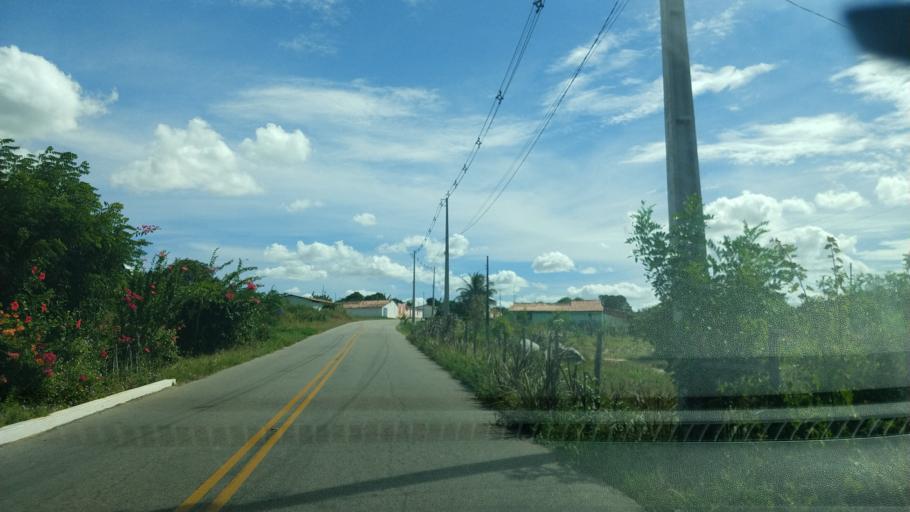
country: BR
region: Rio Grande do Norte
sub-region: Sao Jose Do Campestre
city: Sao Jose do Campestre
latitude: -6.4225
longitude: -35.7341
